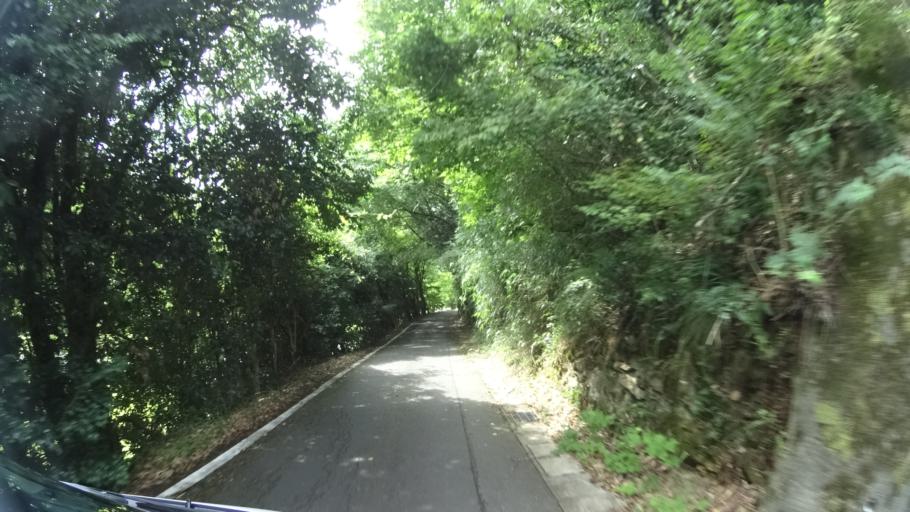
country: JP
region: Kyoto
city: Fukuchiyama
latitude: 35.3669
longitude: 135.1690
